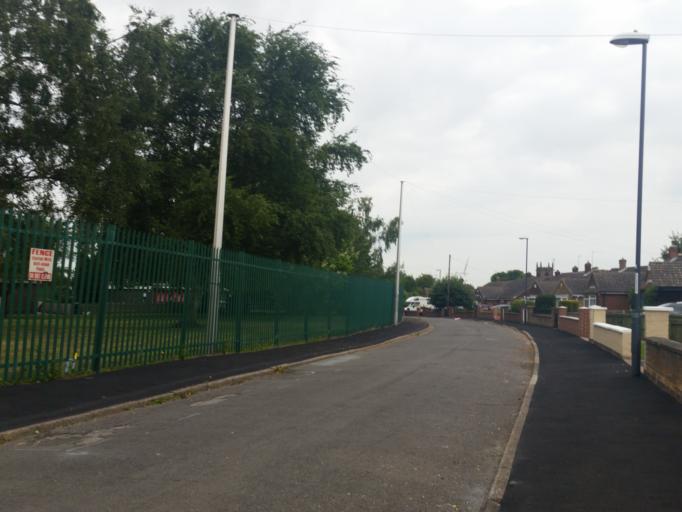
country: GB
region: England
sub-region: Derbyshire
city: Borrowash
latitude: 52.8932
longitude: -1.4193
